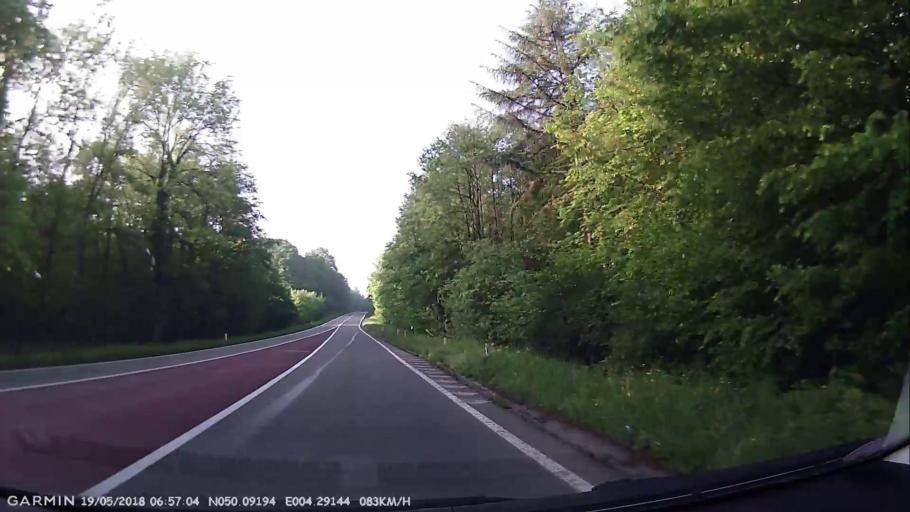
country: BE
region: Wallonia
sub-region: Province du Hainaut
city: Chimay
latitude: 50.0916
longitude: 4.2916
